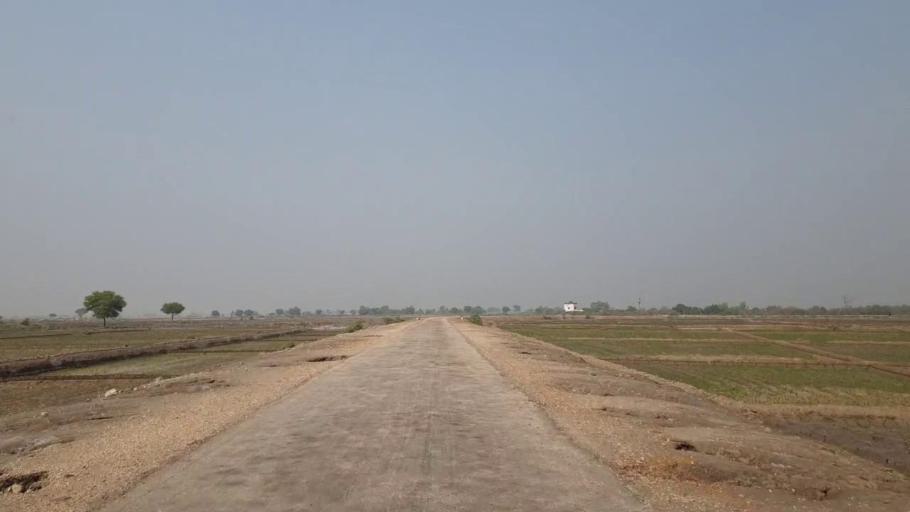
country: PK
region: Sindh
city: Bhan
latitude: 26.4859
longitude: 67.7005
